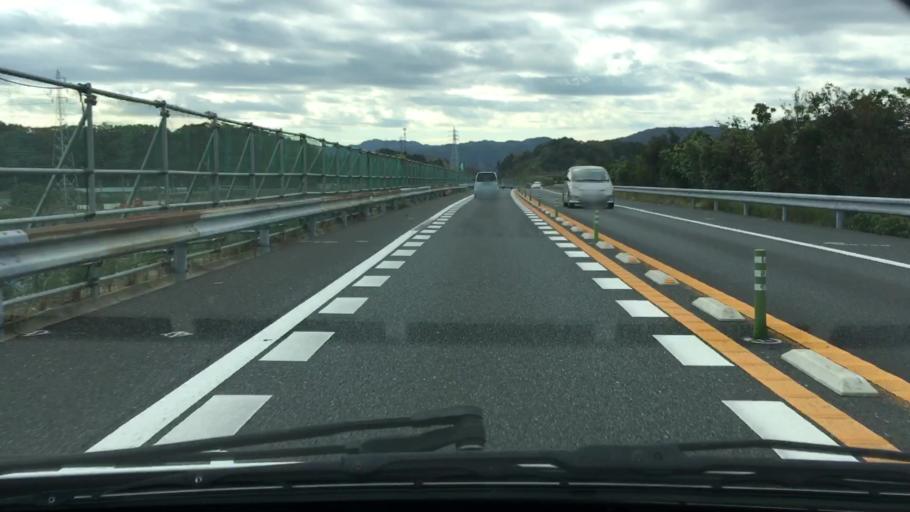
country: JP
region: Chiba
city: Kimitsu
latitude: 35.2360
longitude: 139.8880
